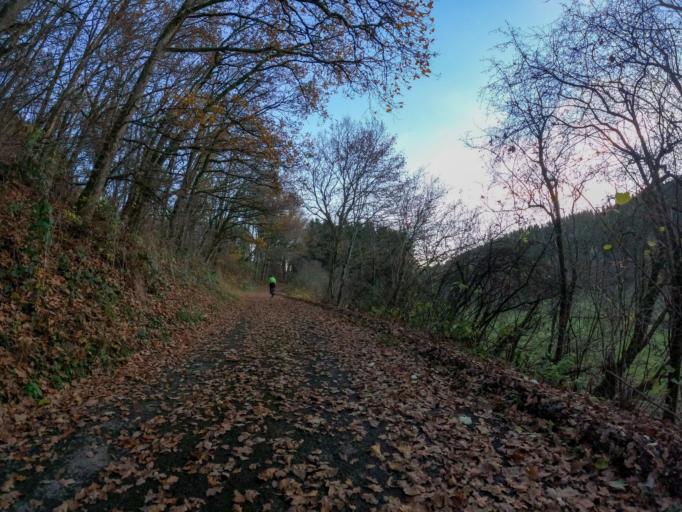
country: LU
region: Diekirch
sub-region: Canton de Wiltz
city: Bavigne
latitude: 49.9287
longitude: 5.8448
